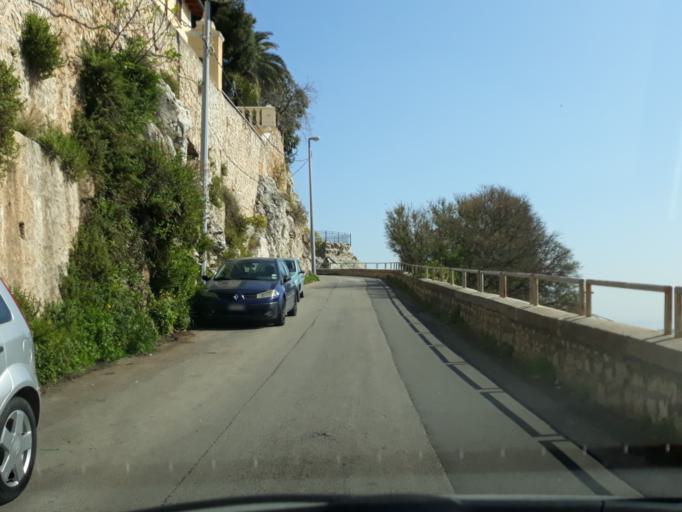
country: IT
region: Sicily
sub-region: Palermo
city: Piano dei Geli
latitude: 38.1093
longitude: 13.3063
